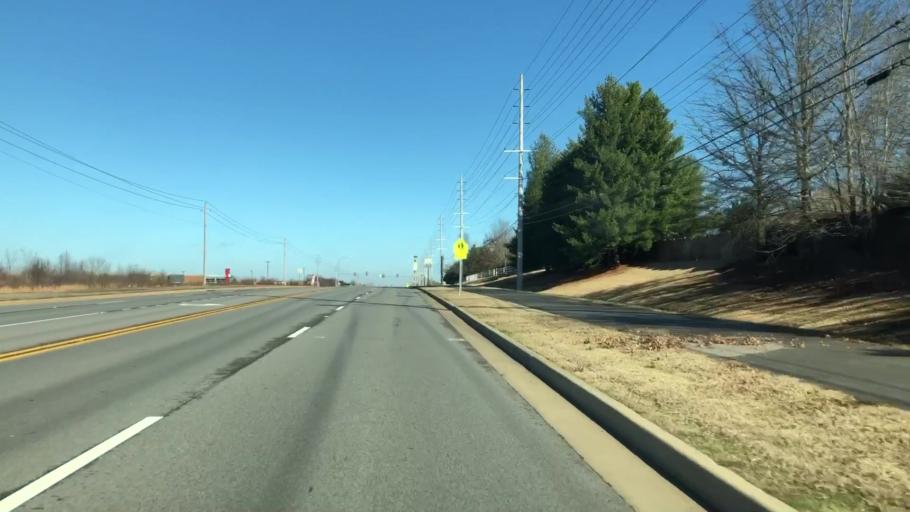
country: US
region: Alabama
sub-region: Madison County
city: Madison
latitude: 34.7031
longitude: -86.7865
